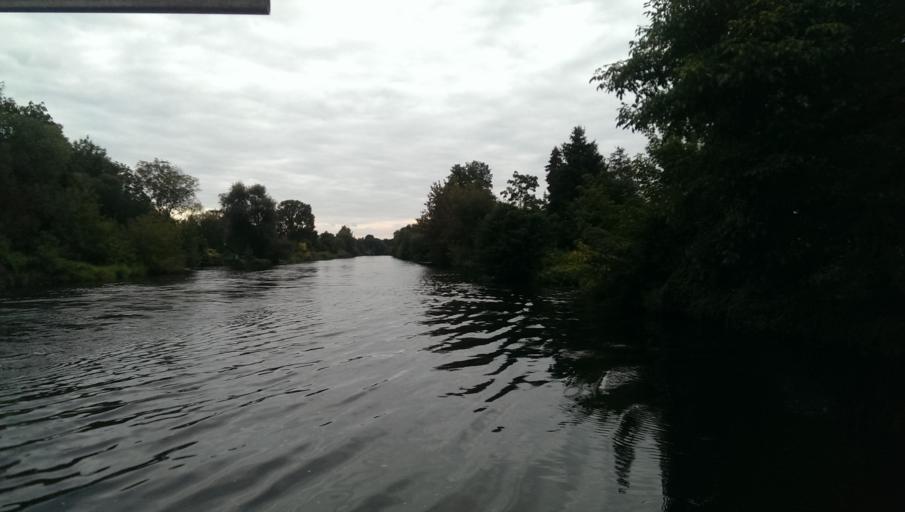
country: DE
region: Brandenburg
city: Oranienburg
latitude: 52.7376
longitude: 13.2558
